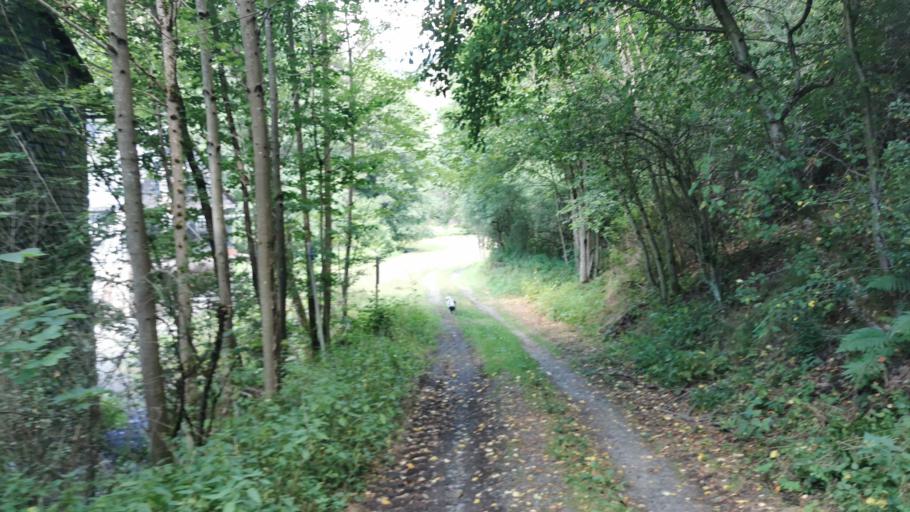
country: DE
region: Thuringia
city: Probstzella
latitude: 50.5155
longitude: 11.4251
